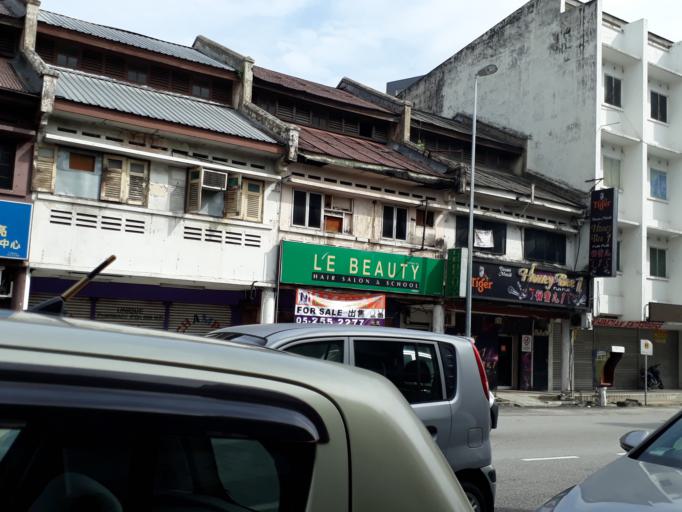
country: MY
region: Perak
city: Ipoh
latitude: 4.5898
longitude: 101.0841
